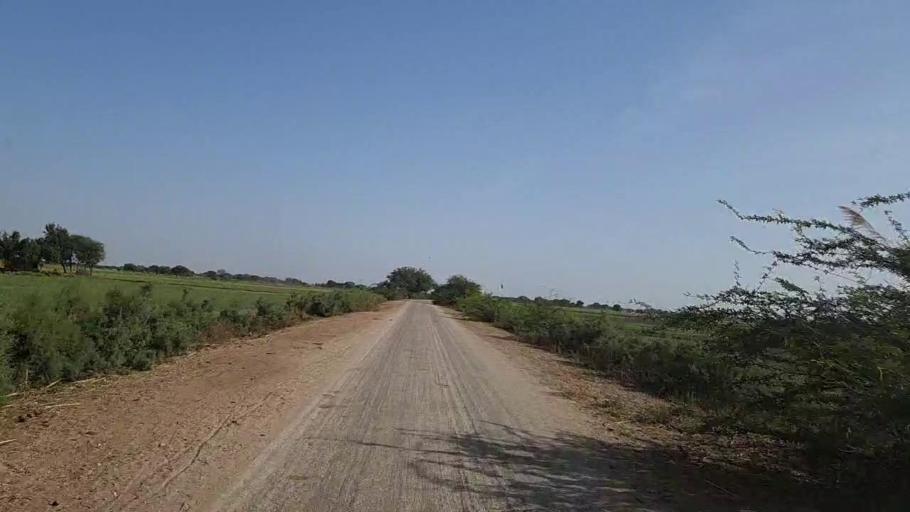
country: PK
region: Sindh
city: Kotri
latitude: 25.1540
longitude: 68.2912
